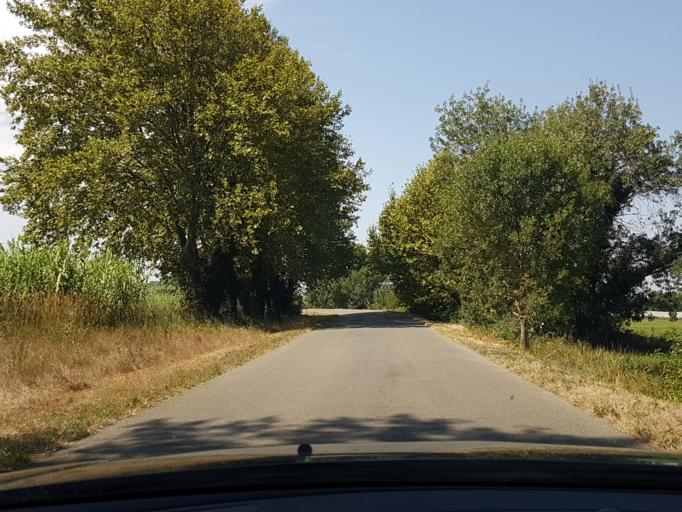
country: FR
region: Provence-Alpes-Cote d'Azur
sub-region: Departement des Bouches-du-Rhone
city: Molleges
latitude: 43.8036
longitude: 4.9077
